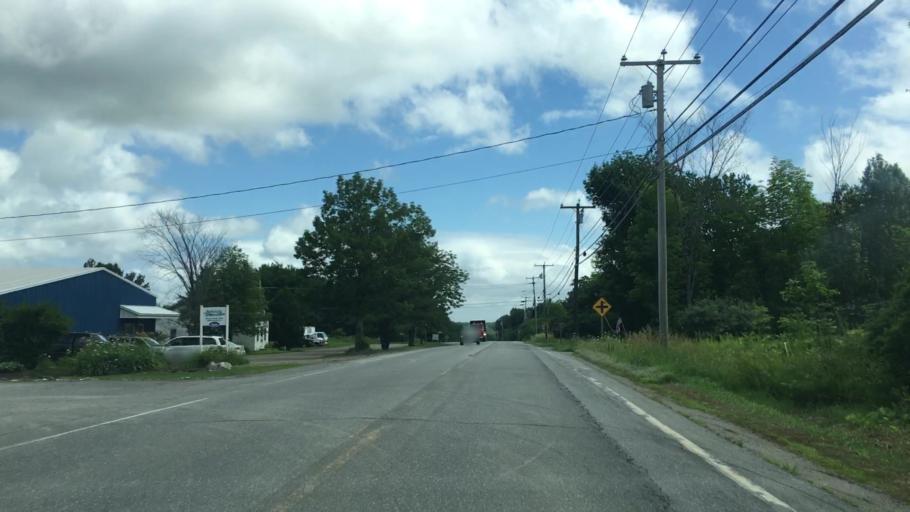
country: US
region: Maine
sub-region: Penobscot County
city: Hermon
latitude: 44.8076
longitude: -68.9315
